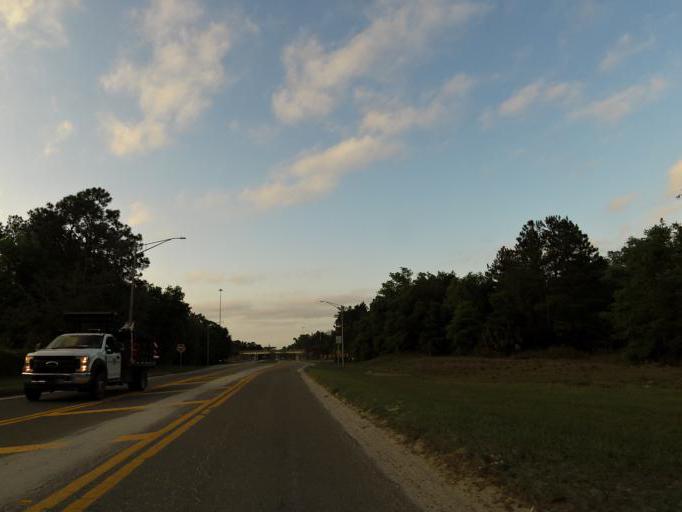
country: US
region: Florida
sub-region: Duval County
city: Jacksonville
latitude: 30.4444
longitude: -81.6130
